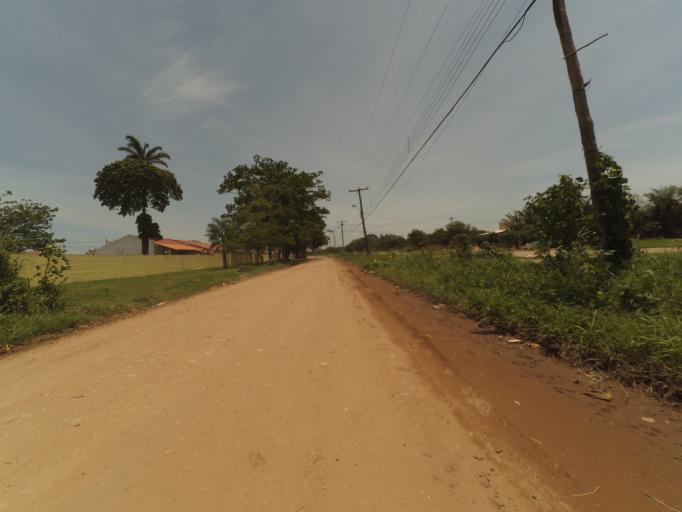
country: BO
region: Santa Cruz
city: Santa Cruz de la Sierra
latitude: -17.8326
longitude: -63.2504
